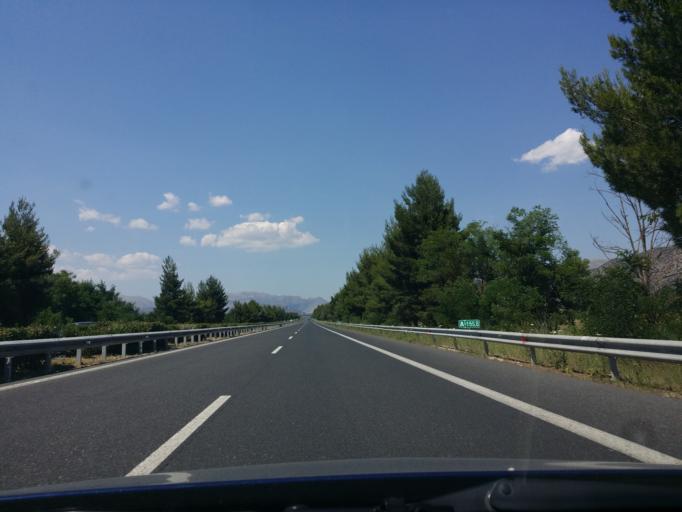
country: GR
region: Peloponnese
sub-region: Nomos Arkadias
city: Tripoli
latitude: 37.5248
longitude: 22.4092
